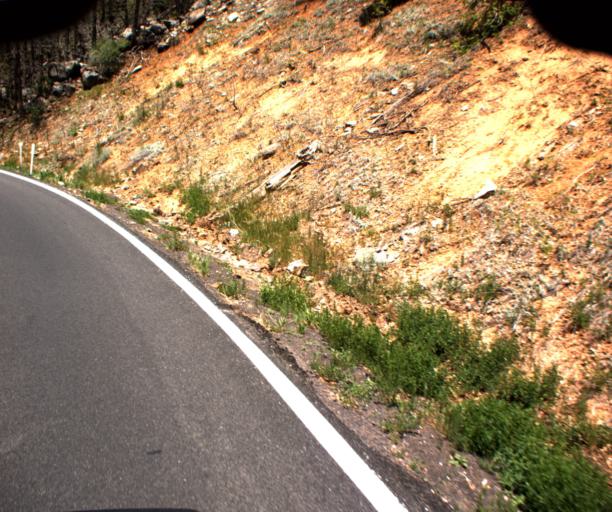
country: US
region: Arizona
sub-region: Coconino County
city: Kachina Village
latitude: 35.0300
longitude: -111.7405
